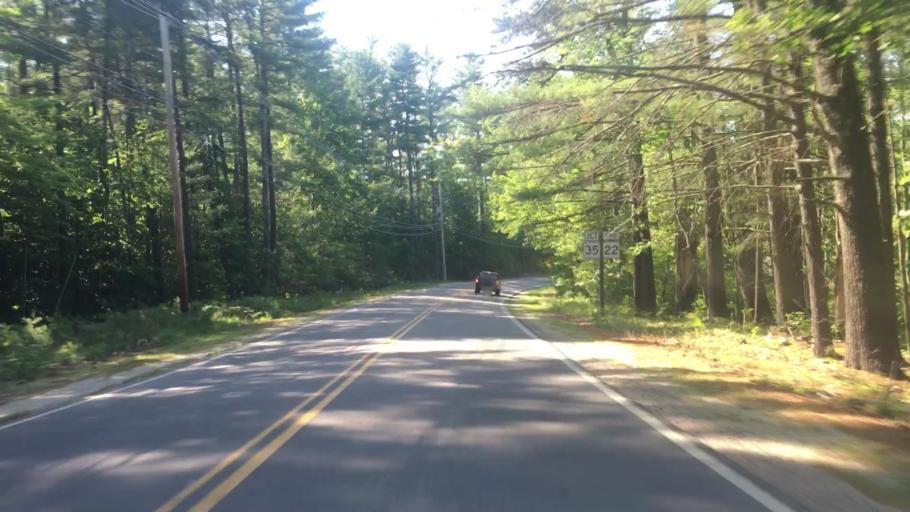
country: US
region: Maine
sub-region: York County
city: Hollis Center
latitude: 43.6905
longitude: -70.5953
